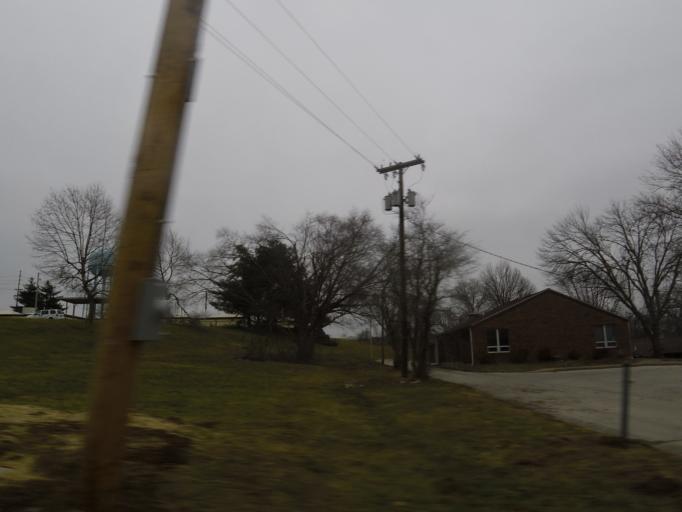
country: US
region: Missouri
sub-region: Marion County
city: Hannibal
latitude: 39.7181
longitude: -91.4005
